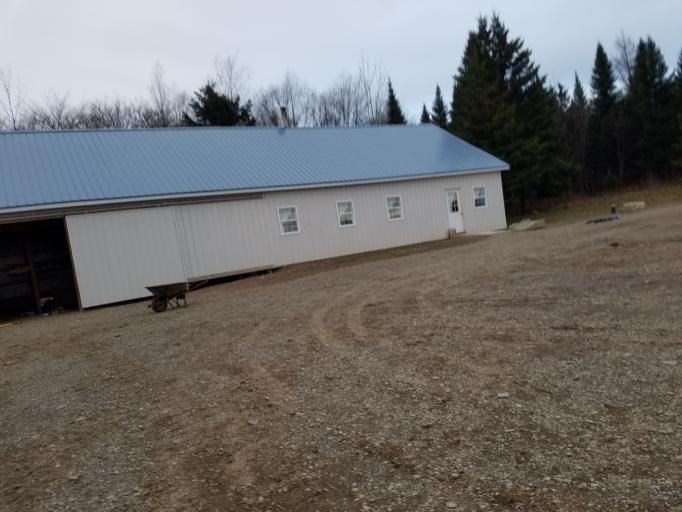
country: US
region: Maine
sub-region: Aroostook County
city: Caribou
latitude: 46.8728
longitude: -68.2172
